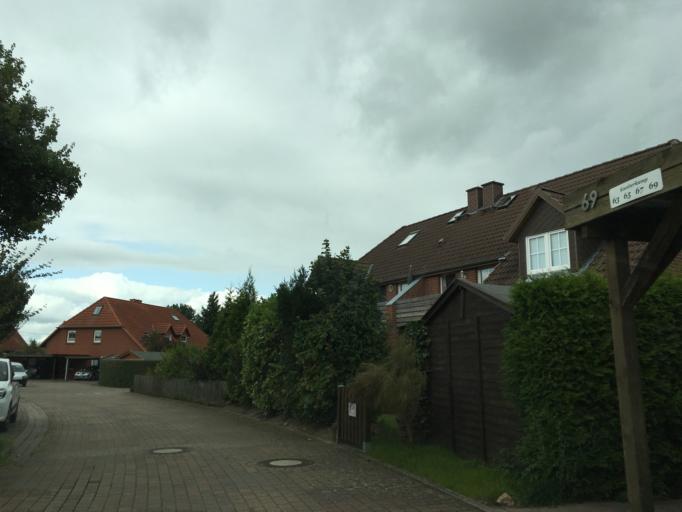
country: DE
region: Lower Saxony
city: Melbeck
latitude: 53.2116
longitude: 10.3771
